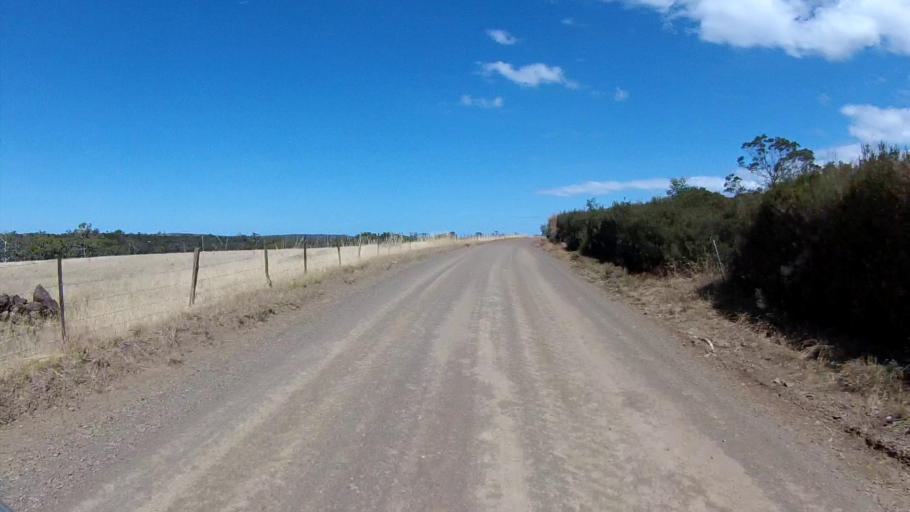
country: AU
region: Tasmania
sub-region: Break O'Day
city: St Helens
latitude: -41.9680
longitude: 148.0741
